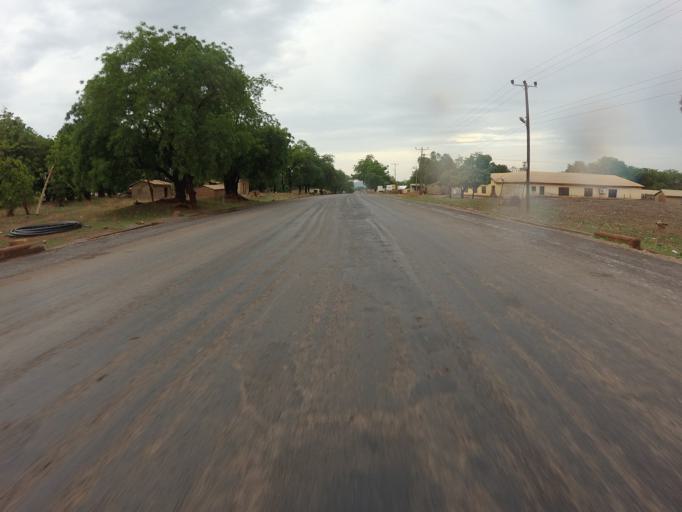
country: GH
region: Upper East
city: Bolgatanga
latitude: 10.8570
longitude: -0.6672
